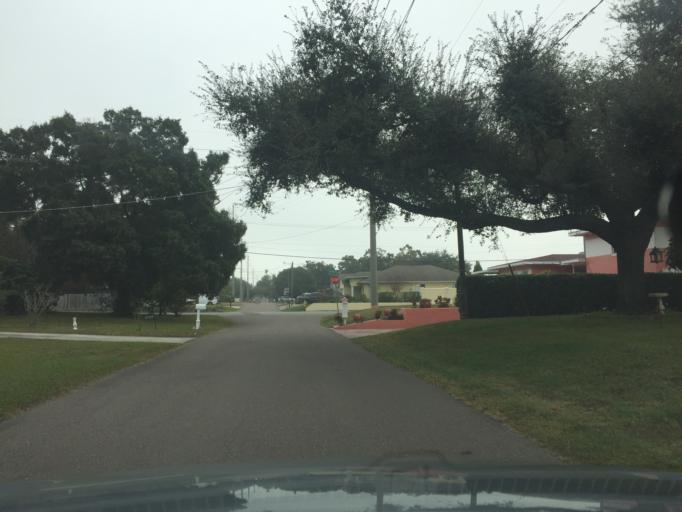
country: US
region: Florida
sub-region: Hillsborough County
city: Tampa
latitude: 27.9535
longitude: -82.4939
